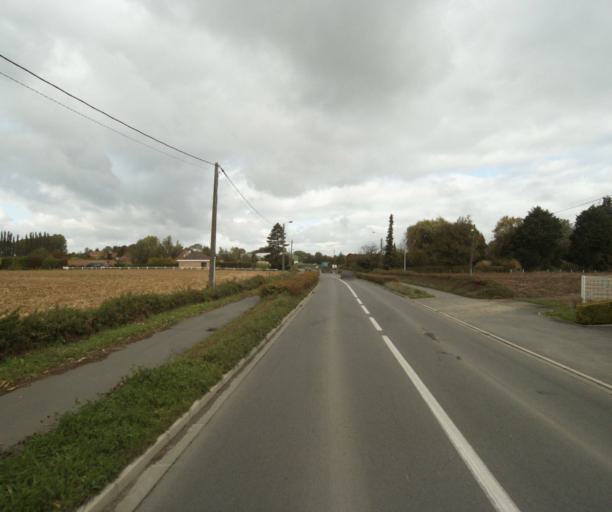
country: FR
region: Nord-Pas-de-Calais
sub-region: Departement du Nord
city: Verlinghem
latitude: 50.6958
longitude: 3.0195
